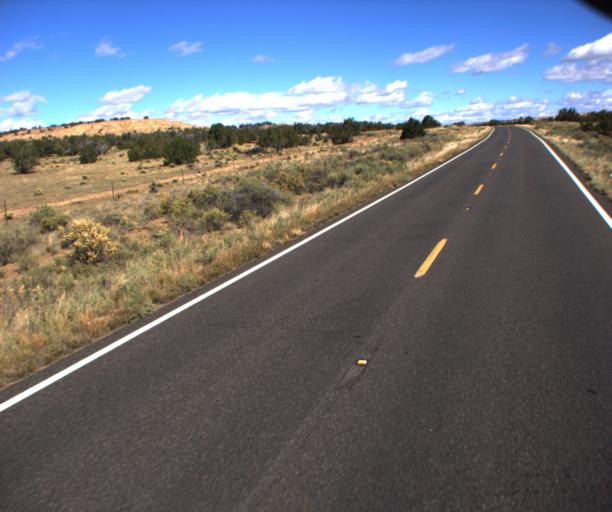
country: US
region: Arizona
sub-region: Apache County
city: Saint Johns
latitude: 34.7790
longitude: -109.2388
